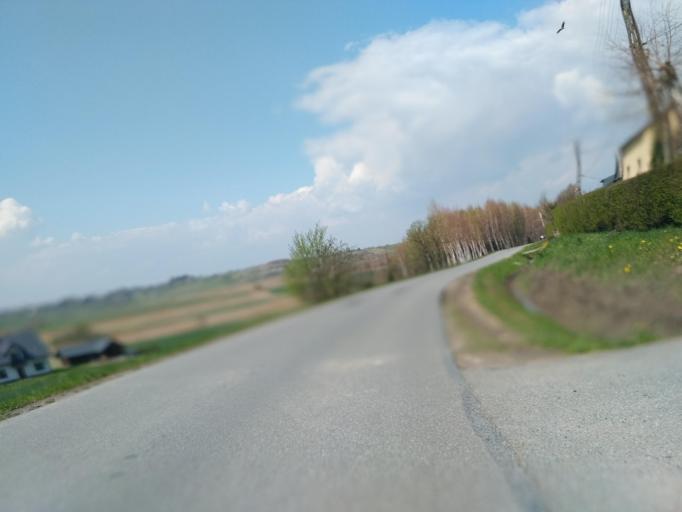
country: PL
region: Subcarpathian Voivodeship
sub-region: Powiat sanocki
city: Nowosielce-Gniewosz
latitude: 49.5425
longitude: 22.1108
